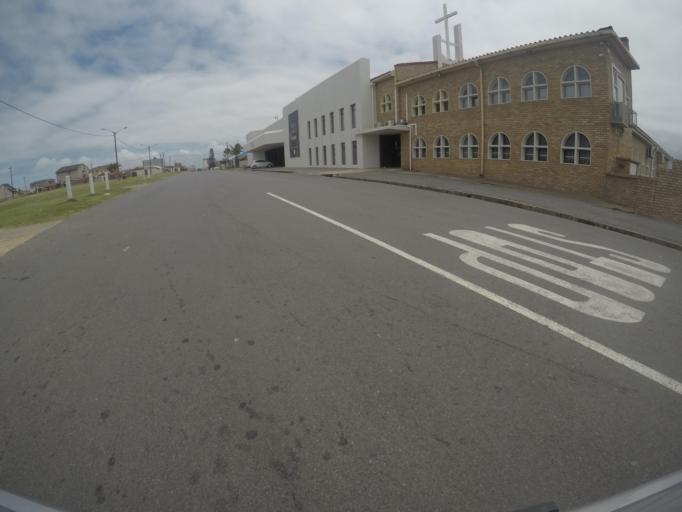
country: ZA
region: Eastern Cape
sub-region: Buffalo City Metropolitan Municipality
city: East London
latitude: -33.0138
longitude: 27.9153
